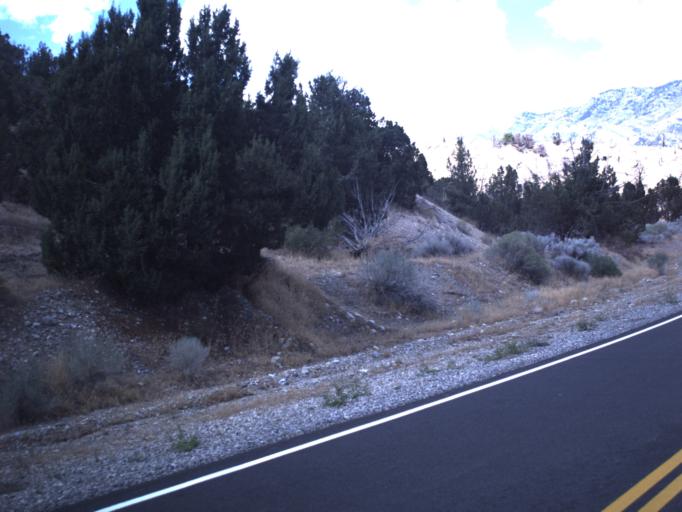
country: US
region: Utah
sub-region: Tooele County
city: Grantsville
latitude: 40.3288
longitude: -112.6207
